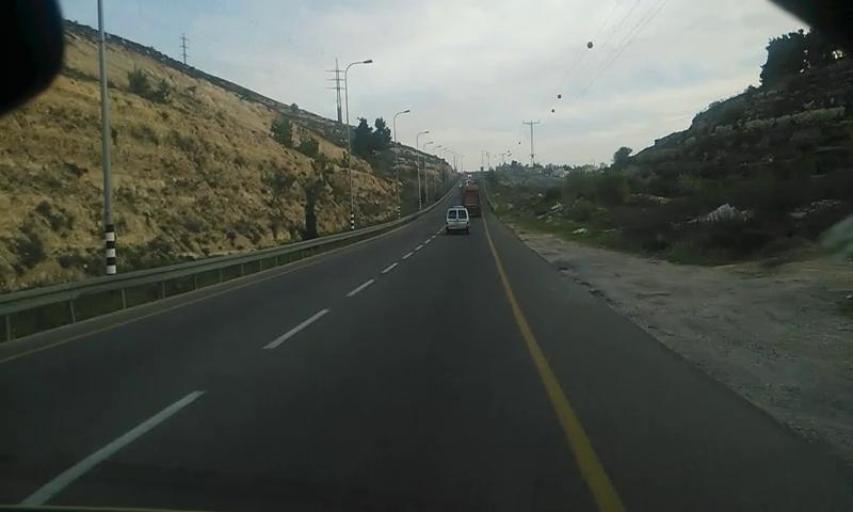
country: PS
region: West Bank
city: Halhul
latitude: 31.5909
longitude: 35.1161
